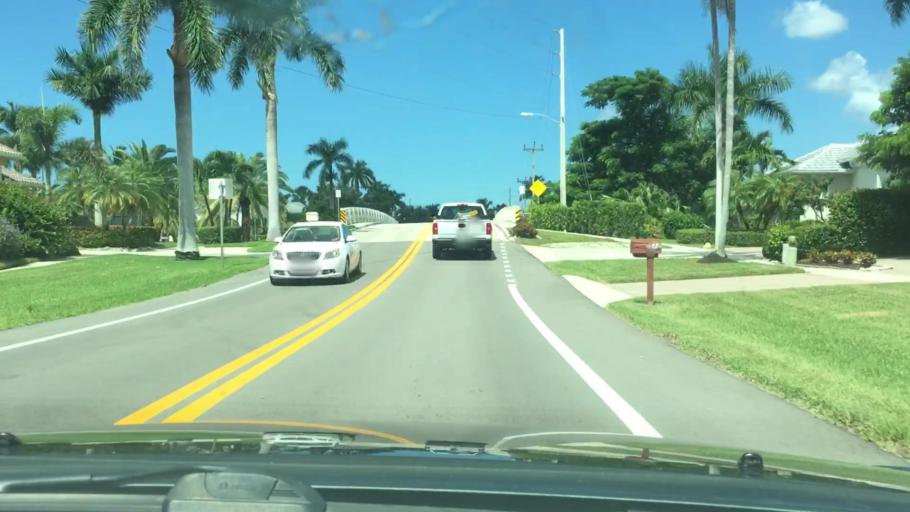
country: US
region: Florida
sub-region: Collier County
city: Marco
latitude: 25.9501
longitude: -81.7370
